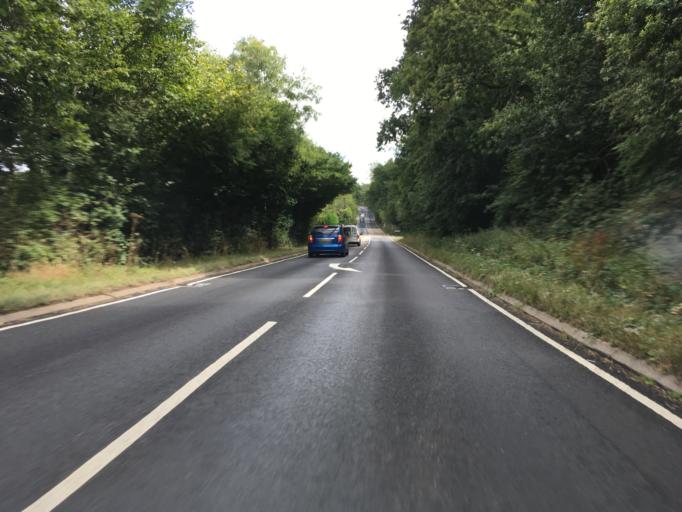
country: GB
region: England
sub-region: Kent
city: Cranbrook
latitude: 51.1127
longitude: 0.5332
